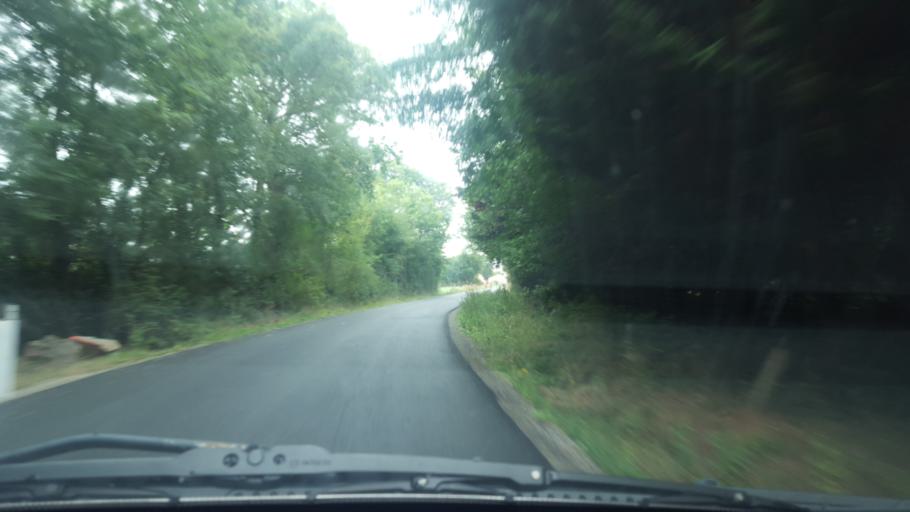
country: FR
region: Pays de la Loire
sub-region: Departement de la Loire-Atlantique
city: Saint-Lumine-de-Coutais
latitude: 47.0500
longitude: -1.6963
